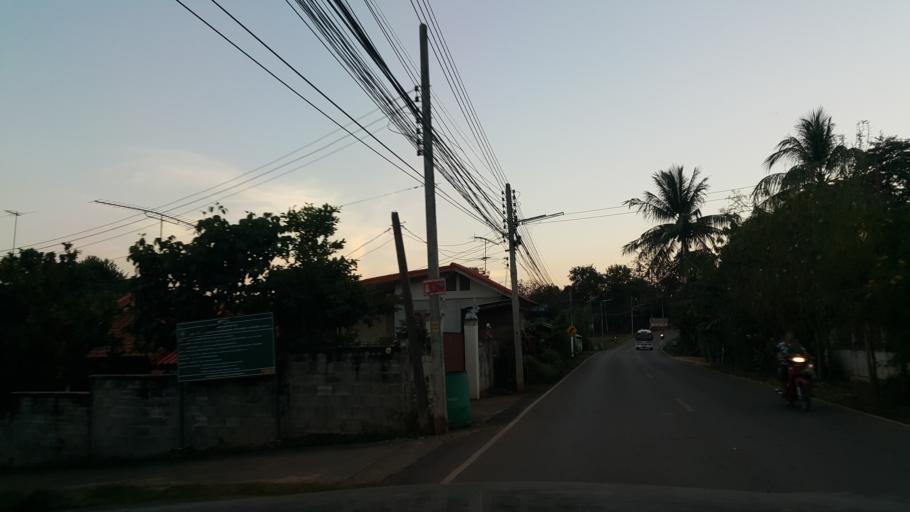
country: TH
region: Uttaradit
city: Uttaradit
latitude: 17.6588
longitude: 100.0933
